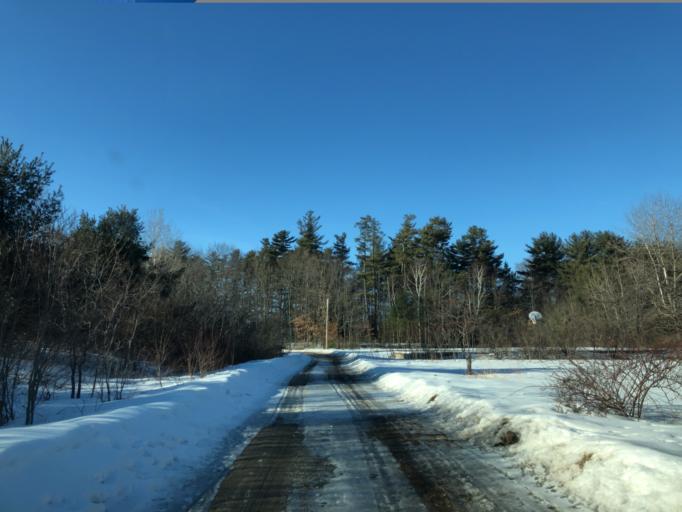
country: US
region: Maine
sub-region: Androscoggin County
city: Poland
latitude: 44.0263
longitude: -70.3596
